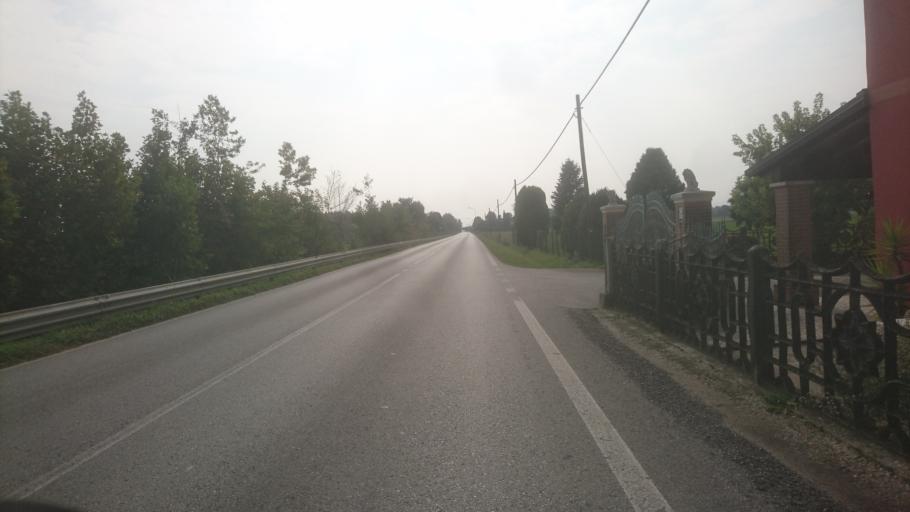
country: IT
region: Veneto
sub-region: Provincia di Vicenza
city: Quinto Vicentino
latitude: 45.5806
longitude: 11.6454
